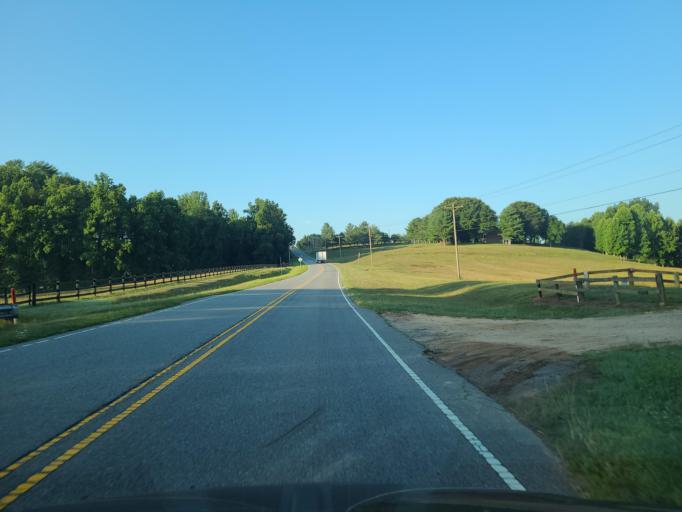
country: US
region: North Carolina
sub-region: Catawba County
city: Mountain View
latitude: 35.6446
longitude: -81.3808
